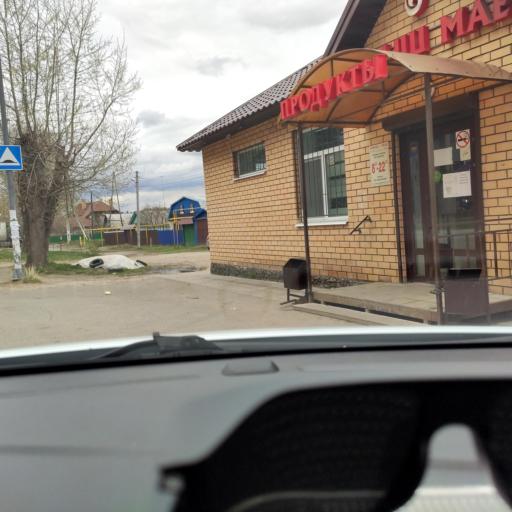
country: RU
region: Tatarstan
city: Vysokaya Gora
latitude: 55.8987
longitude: 49.2511
